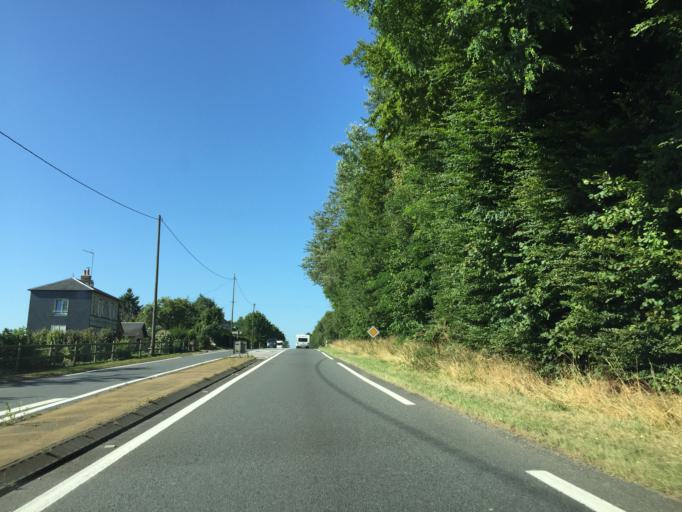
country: FR
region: Lower Normandy
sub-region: Departement du Calvados
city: Lisieux
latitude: 49.2384
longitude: 0.2224
